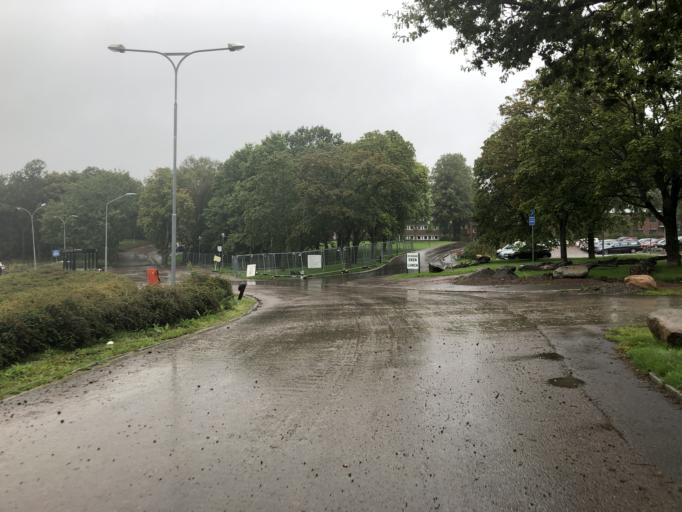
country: SE
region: Vaestra Goetaland
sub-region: Goteborg
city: Goeteborg
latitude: 57.7576
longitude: 11.9497
